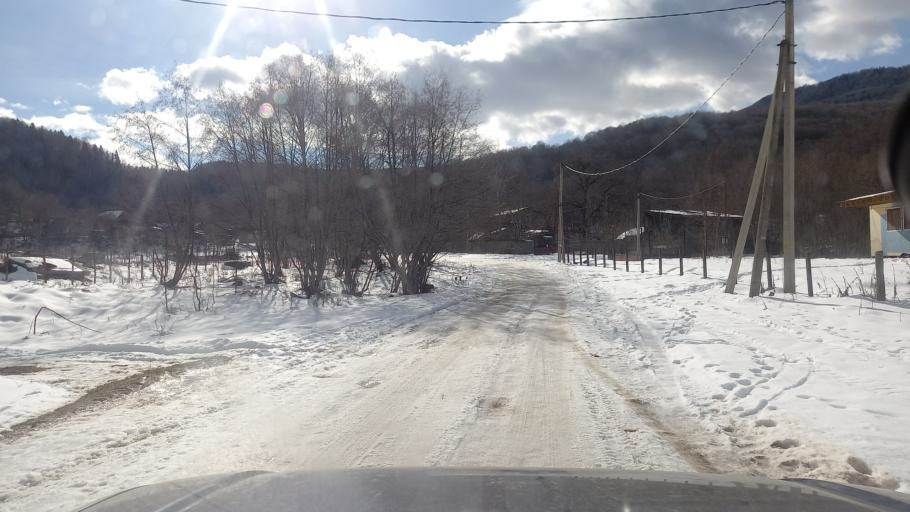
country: RU
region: Adygeya
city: Kamennomostskiy
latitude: 44.1948
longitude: 39.9608
